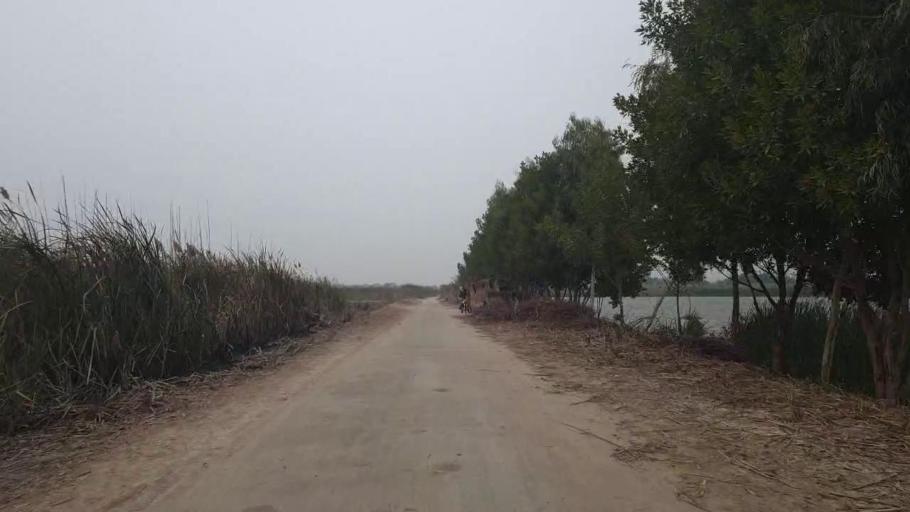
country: PK
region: Sindh
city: Tando Adam
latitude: 25.8400
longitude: 68.6570
